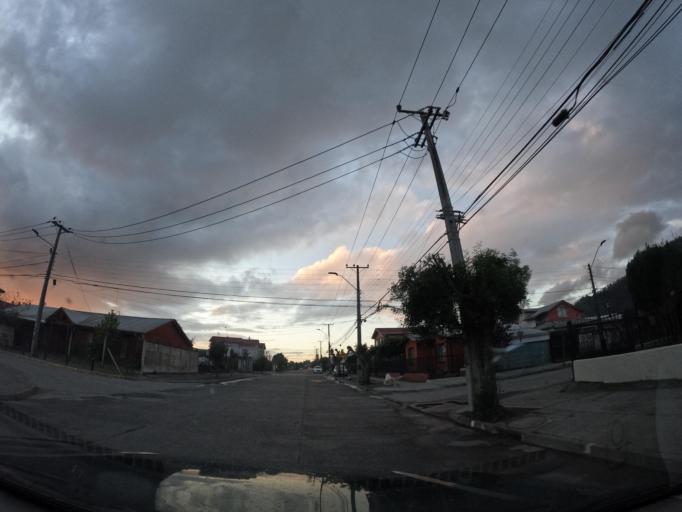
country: CL
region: Biobio
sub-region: Provincia de Concepcion
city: Chiguayante
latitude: -36.9294
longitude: -73.0264
